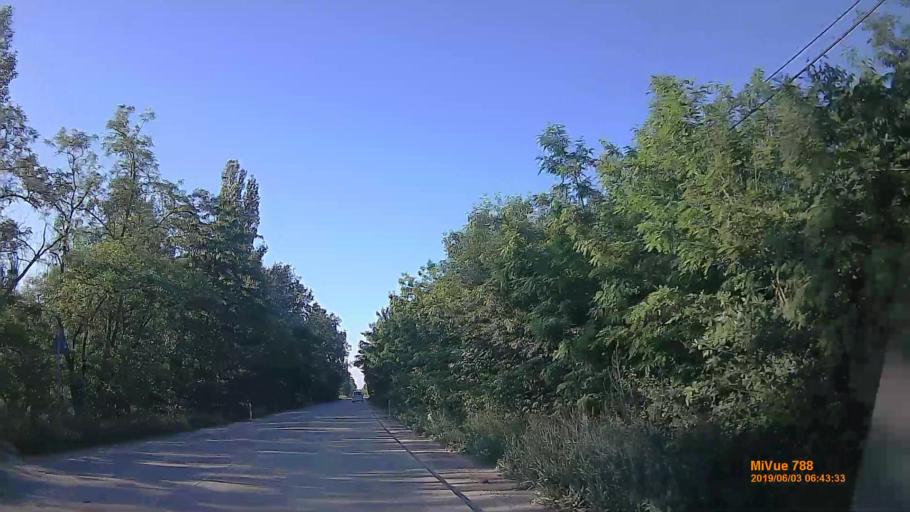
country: HU
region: Pest
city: Bugyi
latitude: 47.2540
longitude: 19.1253
